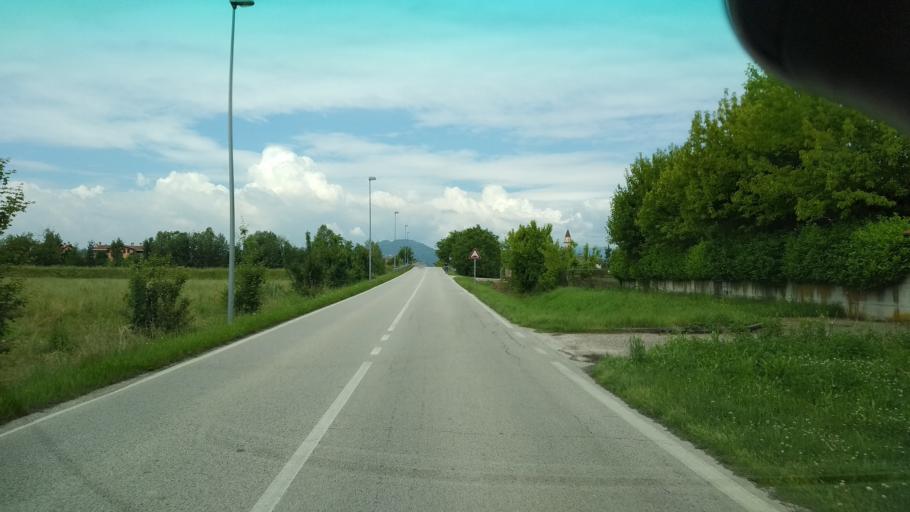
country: IT
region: Veneto
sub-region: Provincia di Vicenza
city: Monticello Conte Otto
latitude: 45.6002
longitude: 11.5389
